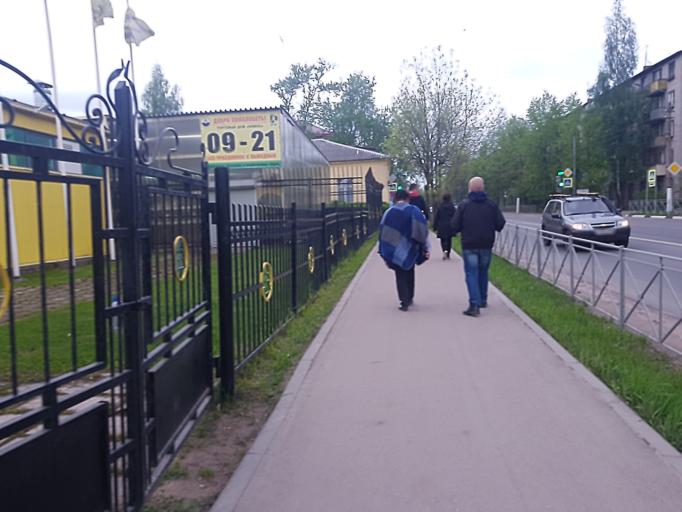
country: RU
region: Leningrad
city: Priozersk
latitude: 61.0343
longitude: 30.1210
